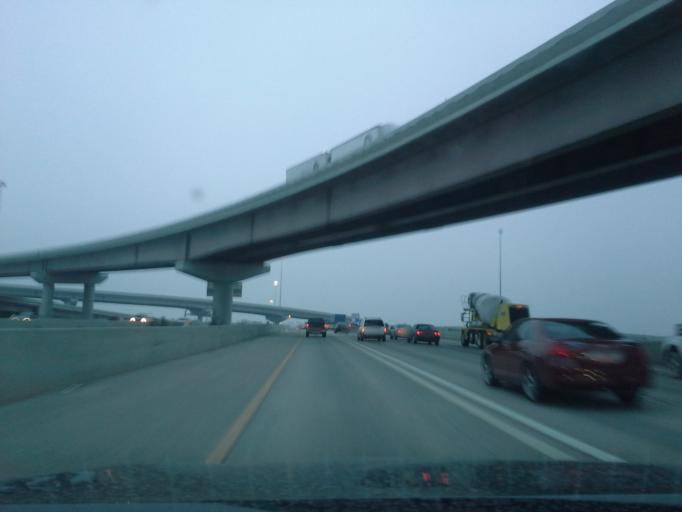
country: US
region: Utah
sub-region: Salt Lake County
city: South Salt Lake
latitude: 40.7207
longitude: -111.9047
